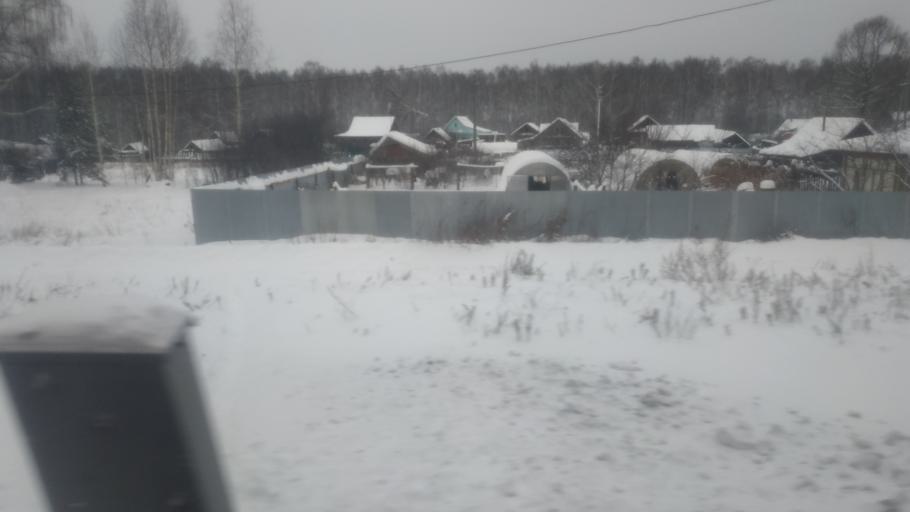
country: RU
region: Udmurtiya
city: Malaya Purga
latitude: 56.5549
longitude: 53.1125
